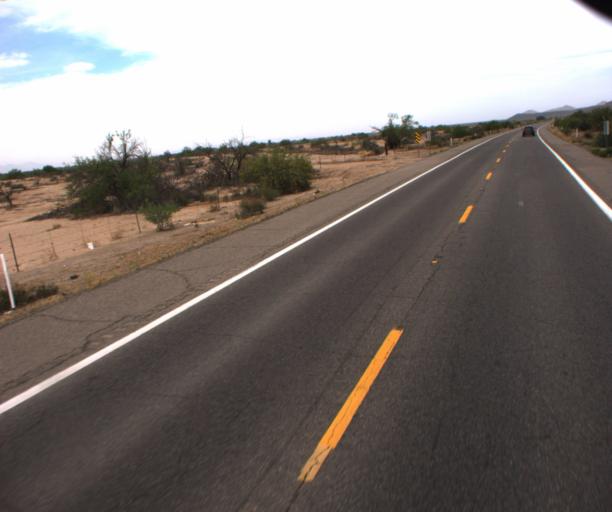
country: US
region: Arizona
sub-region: Pinal County
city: Sacaton
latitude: 33.0781
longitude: -111.7036
